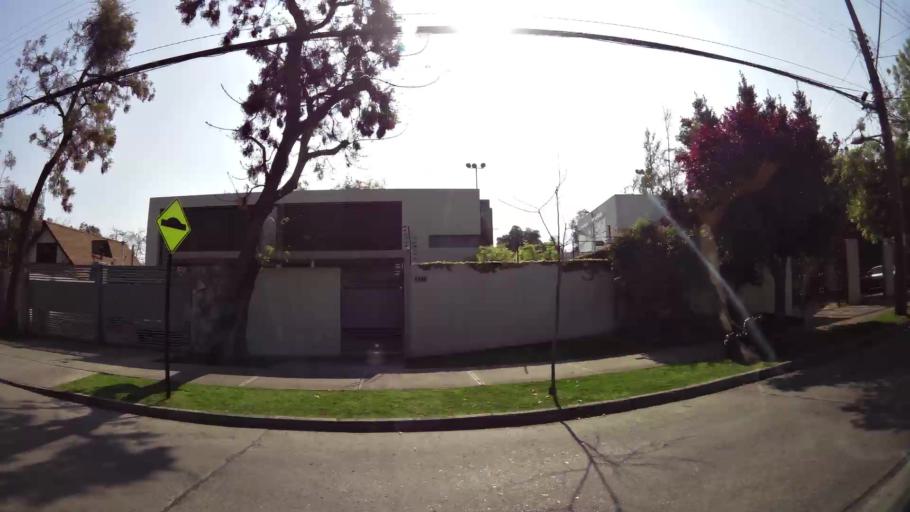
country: CL
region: Santiago Metropolitan
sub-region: Provincia de Santiago
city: Villa Presidente Frei, Nunoa, Santiago, Chile
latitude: -33.3819
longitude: -70.5596
